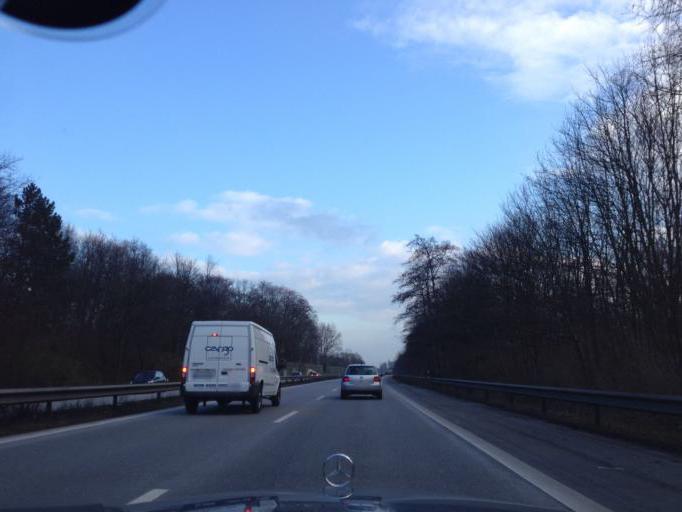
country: DE
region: Hamburg
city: Wandsbek
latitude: 53.5363
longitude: 10.1073
